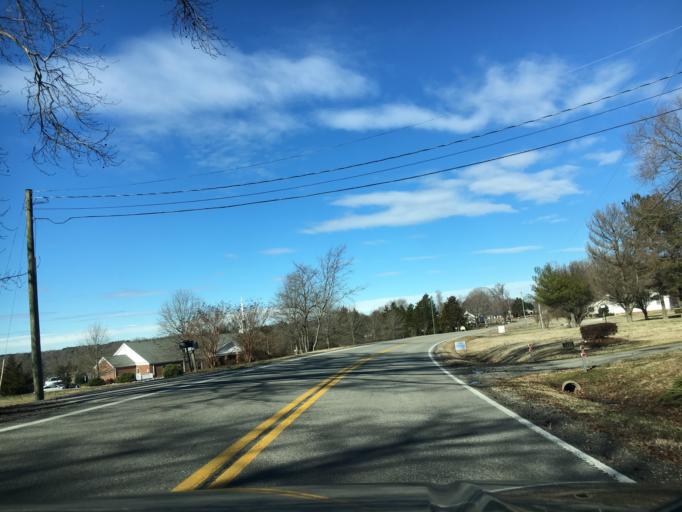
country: US
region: Virginia
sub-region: Halifax County
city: South Boston
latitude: 36.7200
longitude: -78.8628
